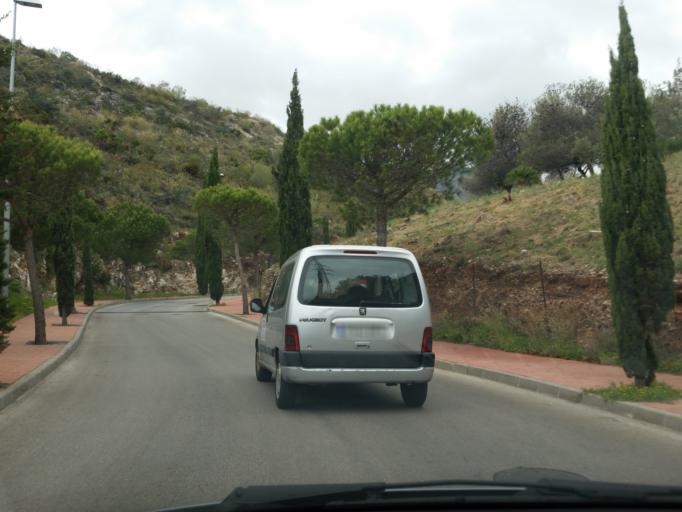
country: ES
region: Andalusia
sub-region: Provincia de Malaga
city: Benalmadena
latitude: 36.6116
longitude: -4.5370
